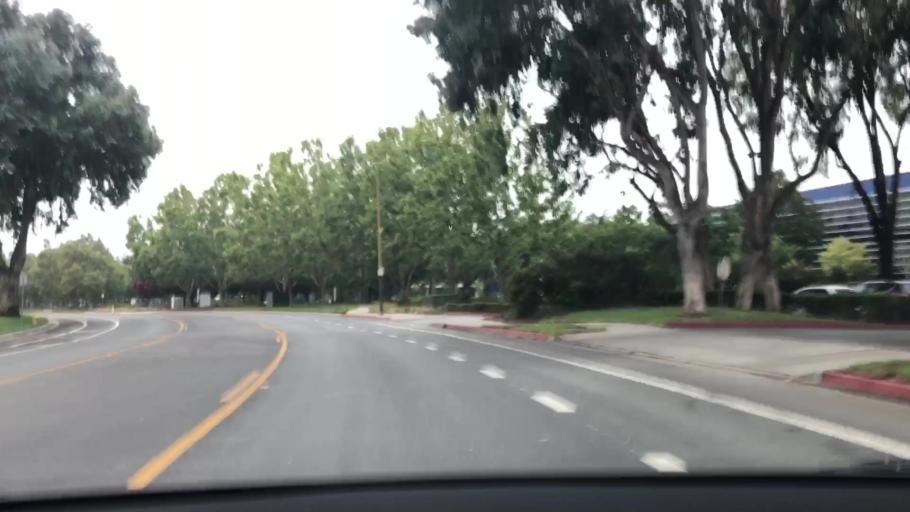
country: US
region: California
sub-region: Santa Clara County
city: Seven Trees
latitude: 37.2374
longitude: -121.7821
